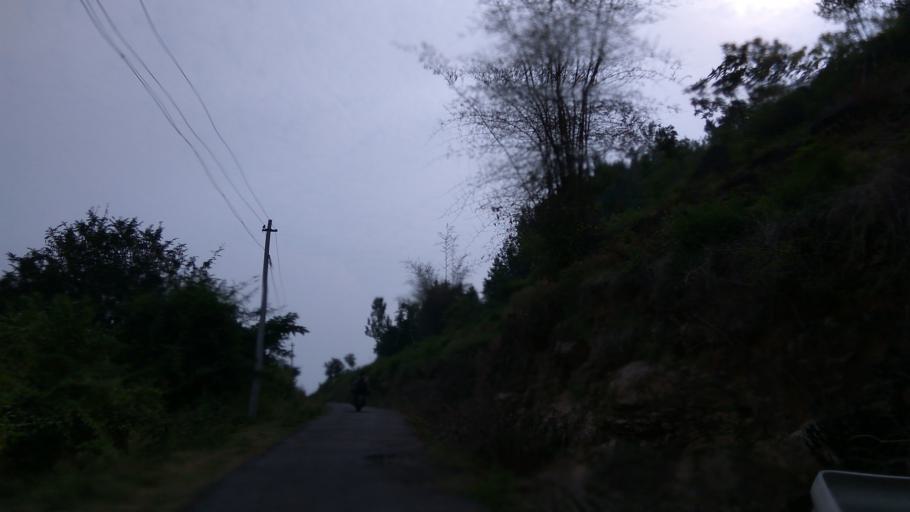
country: IN
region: Tamil Nadu
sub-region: Dharmapuri
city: Mallapuram
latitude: 11.8691
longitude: 78.1946
